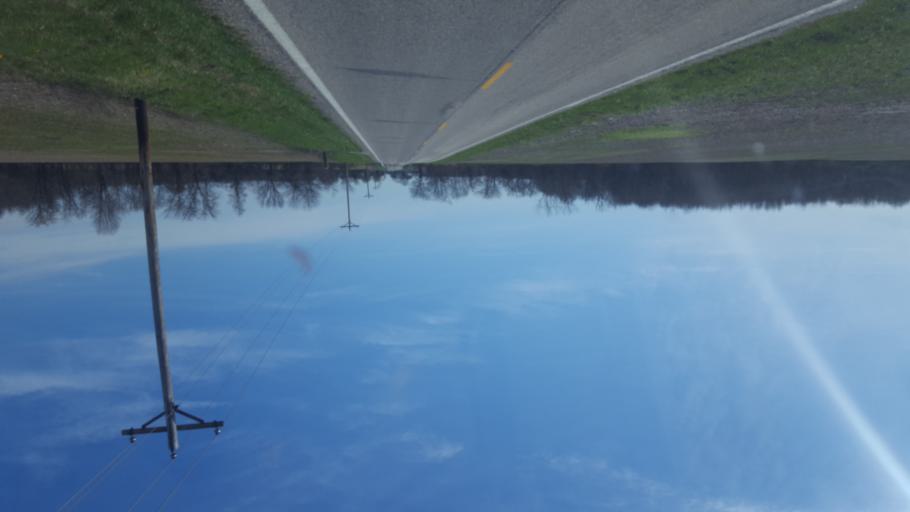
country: US
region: Ohio
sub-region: Morrow County
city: Cardington
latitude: 40.5766
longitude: -82.9623
